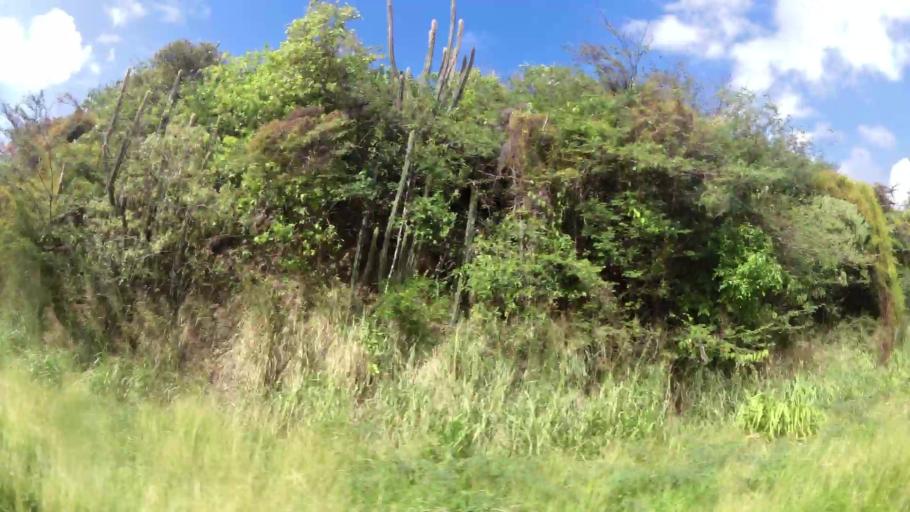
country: MQ
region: Martinique
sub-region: Martinique
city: Le Marin
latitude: 14.4223
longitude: -60.8756
